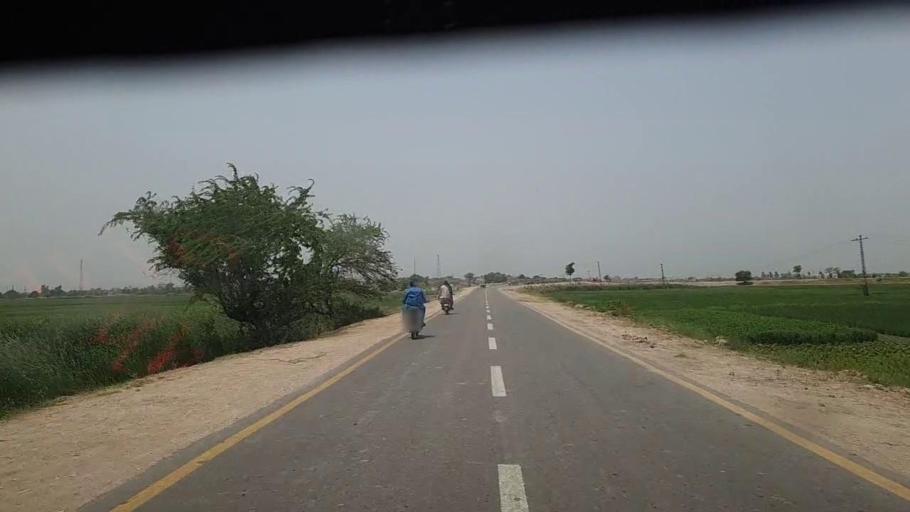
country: PK
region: Sindh
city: Sita Road
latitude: 27.0411
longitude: 67.8619
